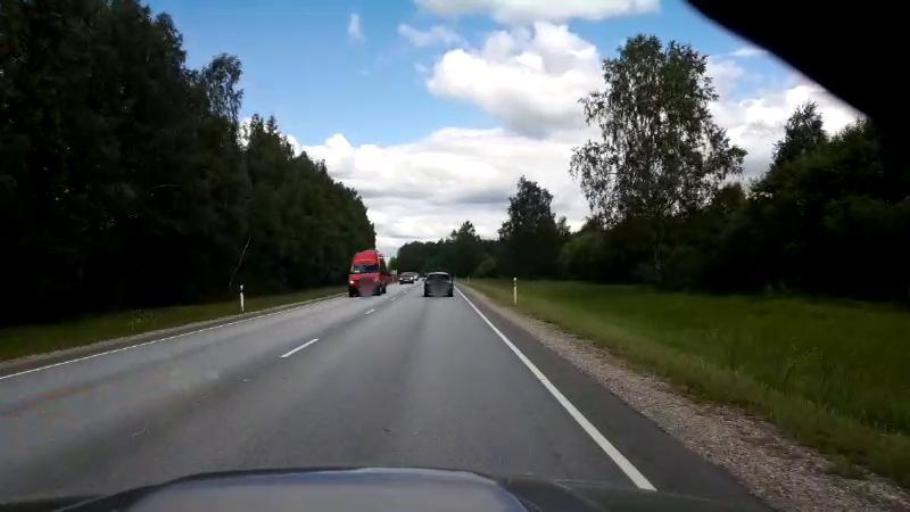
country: EE
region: Paernumaa
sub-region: Sauga vald
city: Sauga
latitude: 58.4560
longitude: 24.5110
